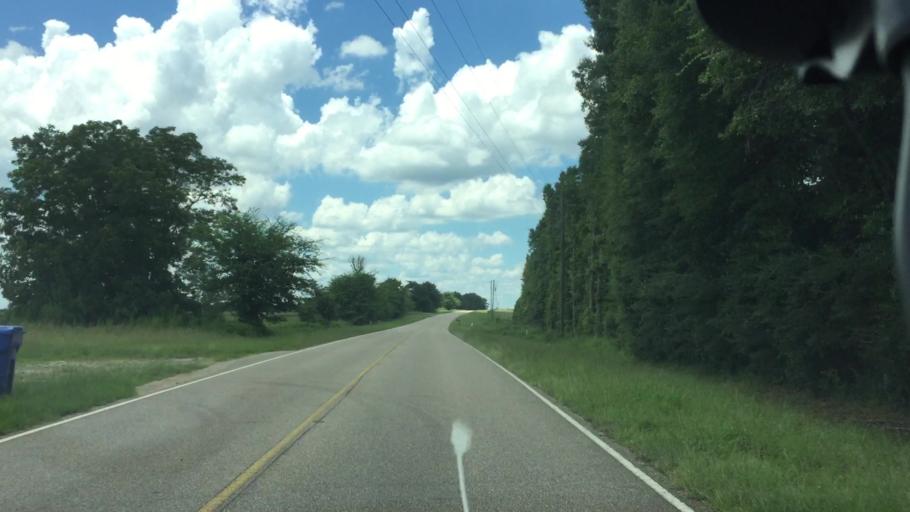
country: US
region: Alabama
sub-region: Coffee County
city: New Brockton
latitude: 31.4143
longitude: -85.8679
